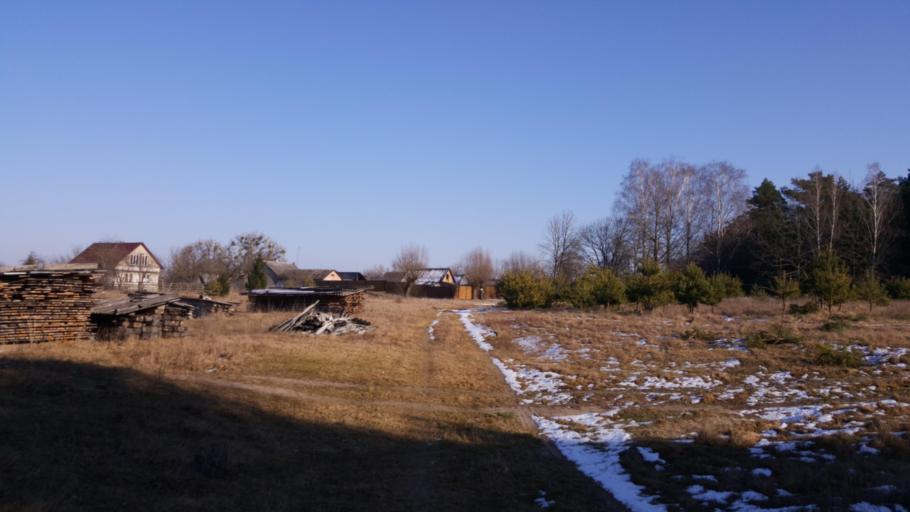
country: BY
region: Brest
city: Kamyanyets
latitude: 52.3852
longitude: 23.7806
